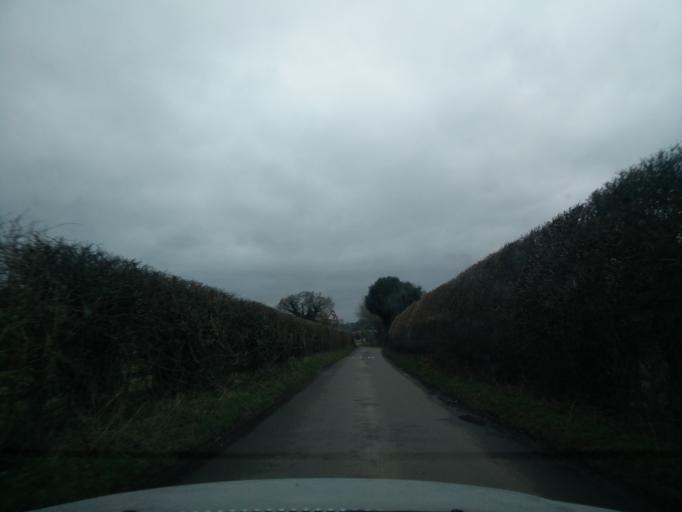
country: GB
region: England
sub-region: Buckinghamshire
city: Great Missenden
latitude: 51.6805
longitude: -0.6704
